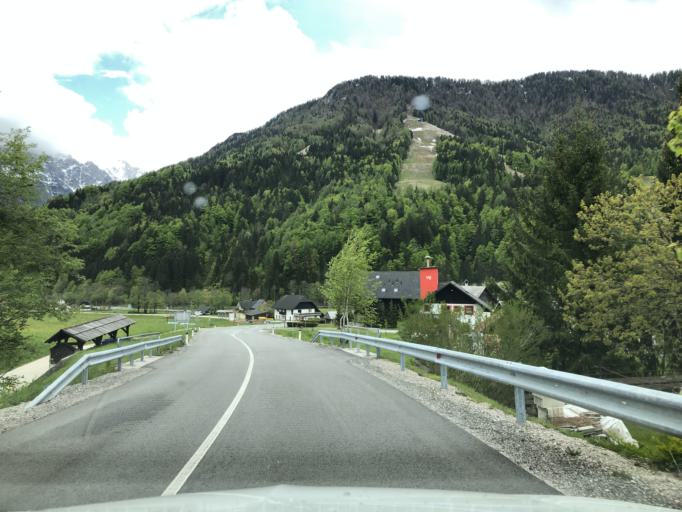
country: SI
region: Kranjska Gora
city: Kranjska Gora
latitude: 46.4941
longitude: 13.7577
